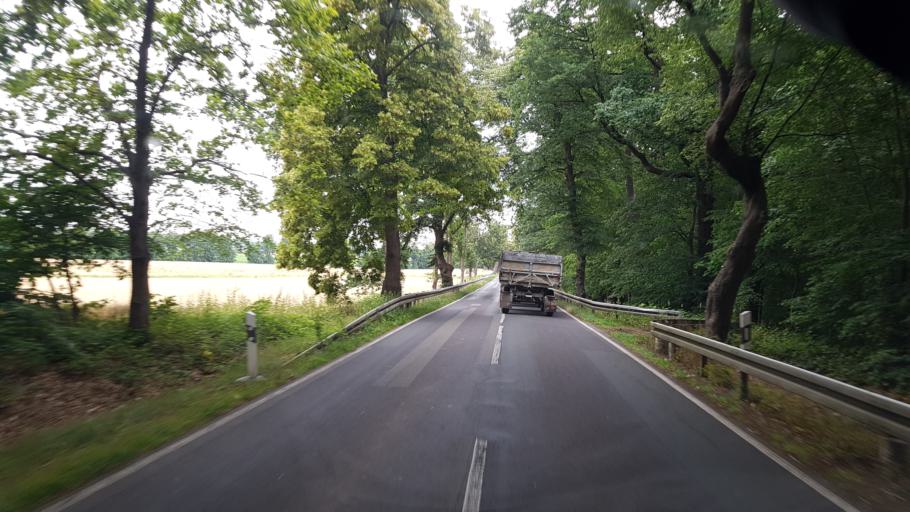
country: DE
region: Brandenburg
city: Lebusa
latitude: 51.7891
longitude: 13.4073
